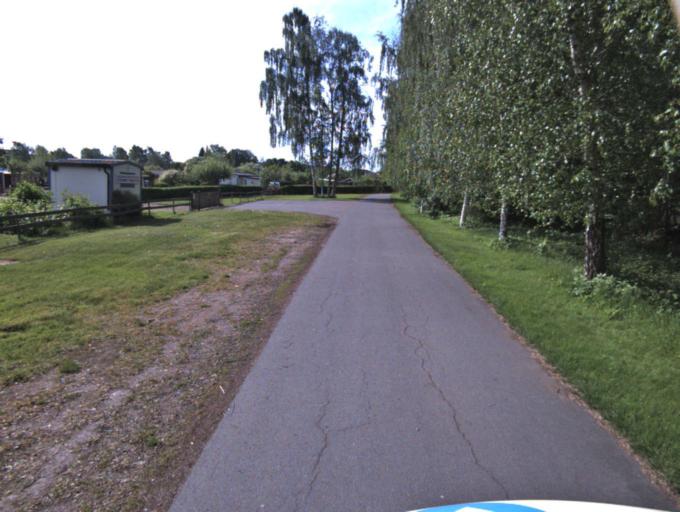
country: SE
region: Skane
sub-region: Kristianstads Kommun
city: Kristianstad
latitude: 56.0329
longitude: 14.1768
